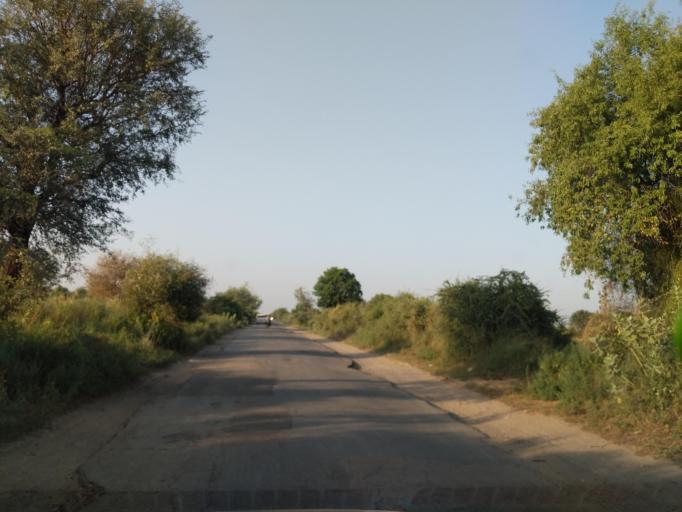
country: IN
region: Rajasthan
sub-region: Churu
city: Rajgarh
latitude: 28.5682
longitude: 75.3679
